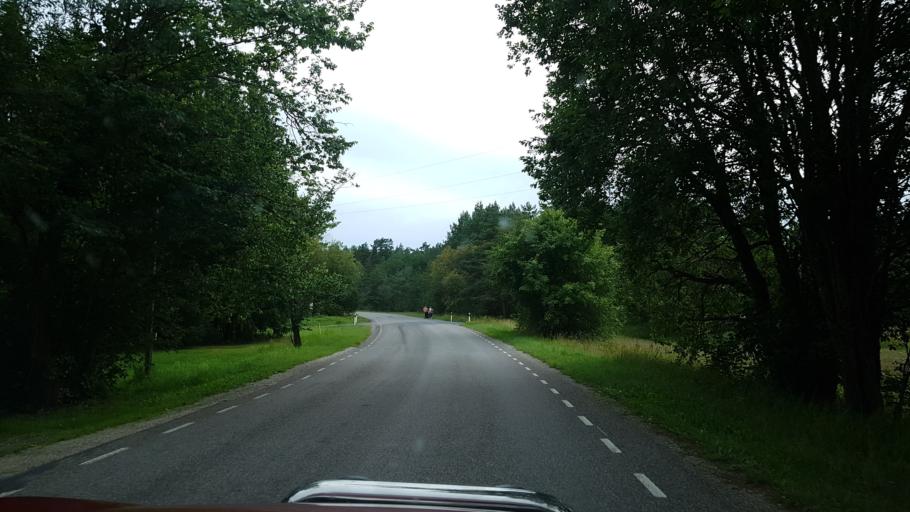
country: EE
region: Laeaene
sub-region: Lihula vald
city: Lihula
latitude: 58.9699
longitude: 23.8951
